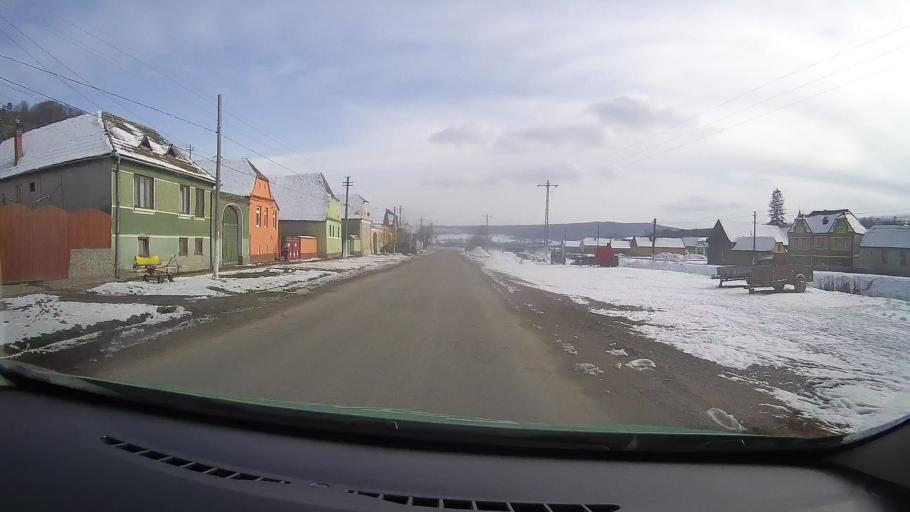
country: RO
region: Sibiu
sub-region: Comuna Iacobeni
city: Iacobeni
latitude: 46.0492
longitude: 24.7201
